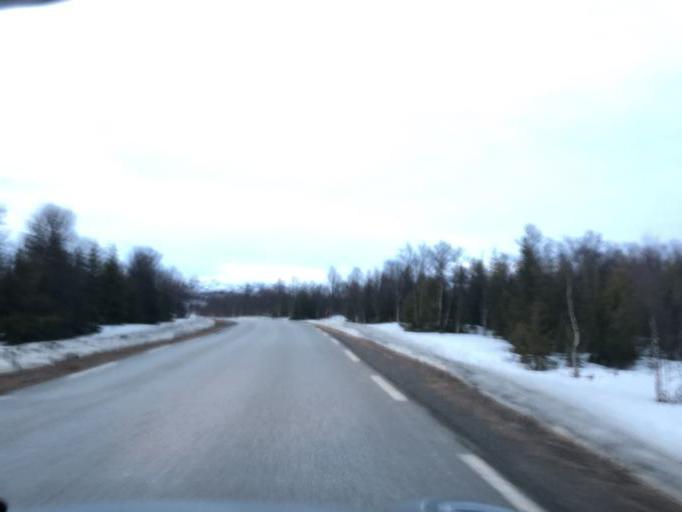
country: NO
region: Sor-Trondelag
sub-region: Tydal
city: Aas
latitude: 62.7200
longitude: 11.8223
